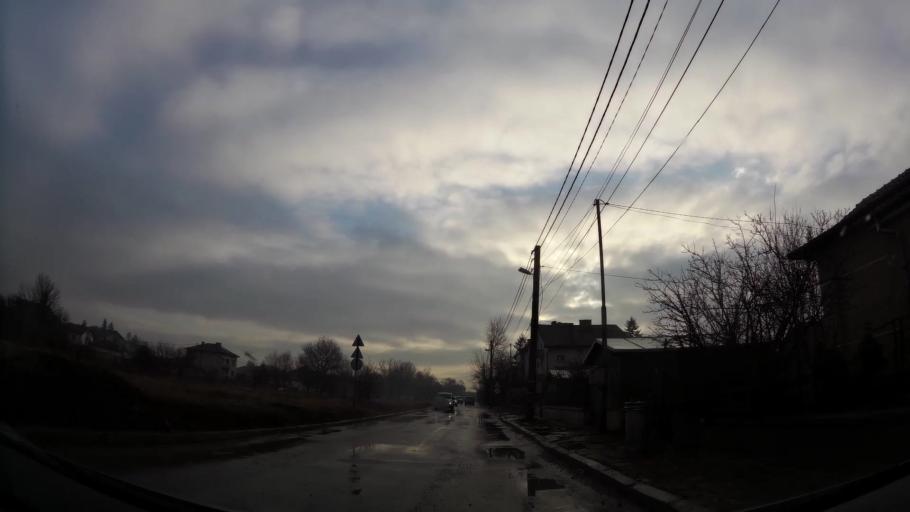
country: BG
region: Sofia-Capital
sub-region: Stolichna Obshtina
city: Sofia
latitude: 42.7375
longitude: 23.3372
